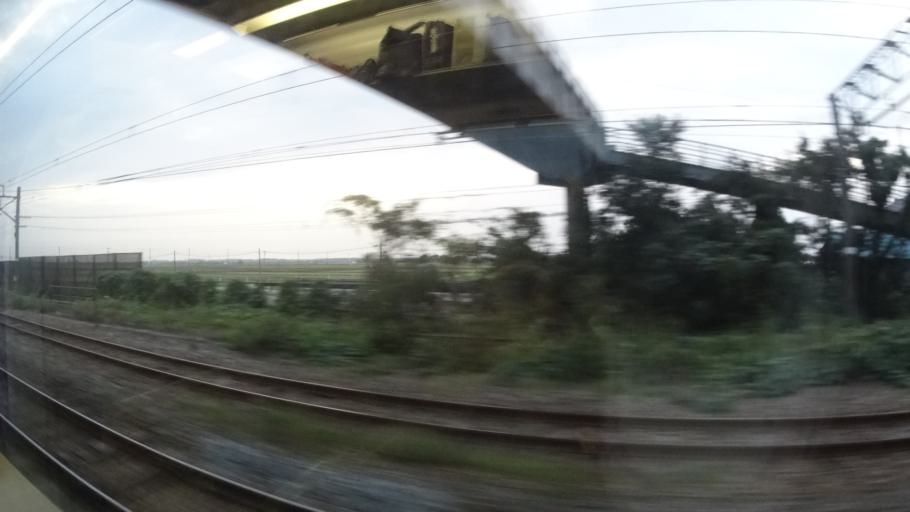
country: JP
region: Niigata
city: Murakami
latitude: 38.1166
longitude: 139.4436
